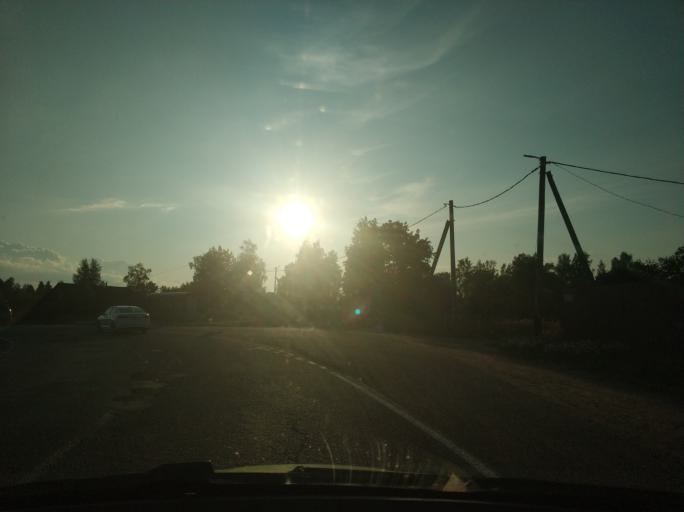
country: RU
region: Leningrad
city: Borisova Griva
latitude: 60.0955
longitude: 30.9684
